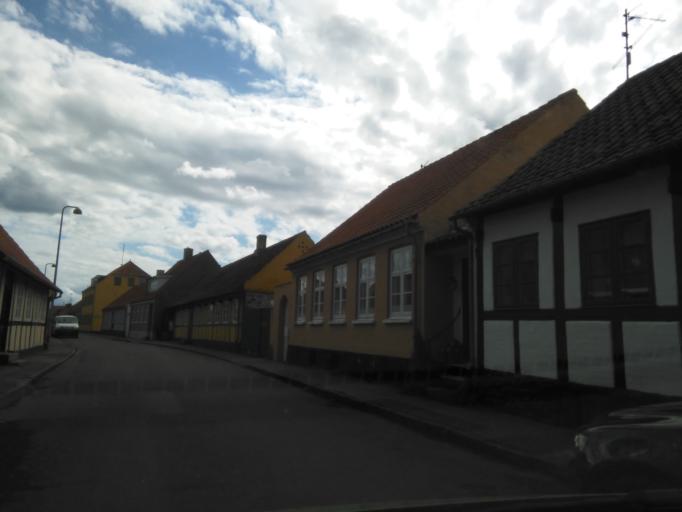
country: DK
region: Capital Region
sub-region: Bornholm Kommune
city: Nexo
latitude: 55.0669
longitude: 15.1332
